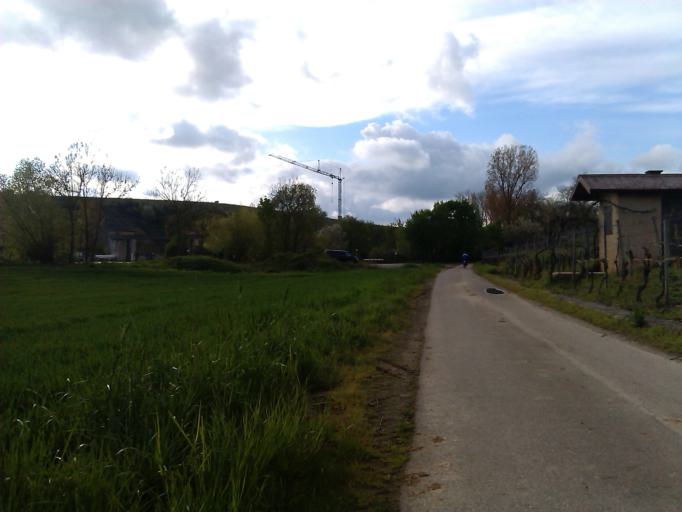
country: DE
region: Baden-Wuerttemberg
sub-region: Regierungsbezirk Stuttgart
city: Lauffen am Neckar
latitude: 49.0981
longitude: 9.1560
